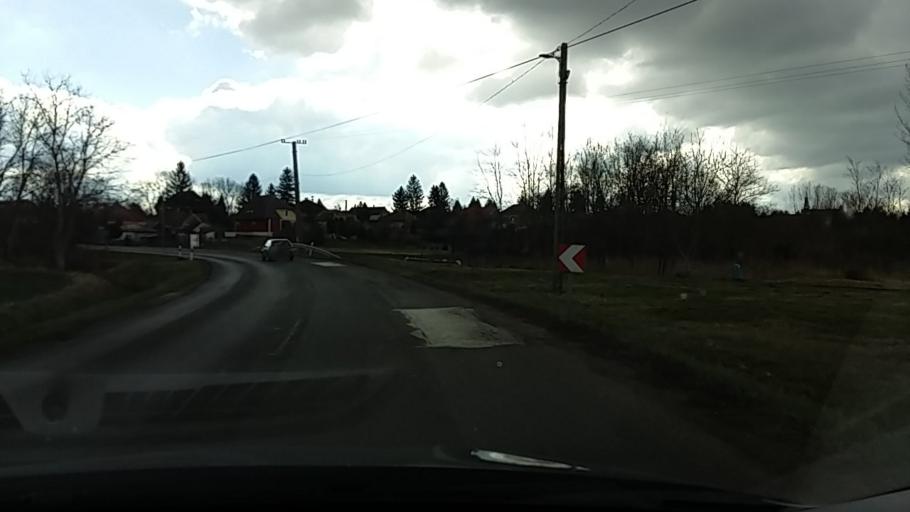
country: HU
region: Somogy
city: Bohonye
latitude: 46.4130
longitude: 17.3842
